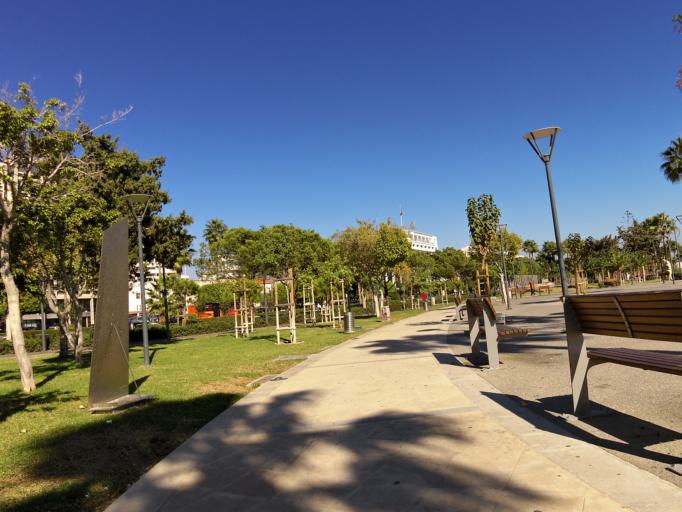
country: CY
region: Limassol
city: Limassol
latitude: 34.6723
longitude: 33.0448
